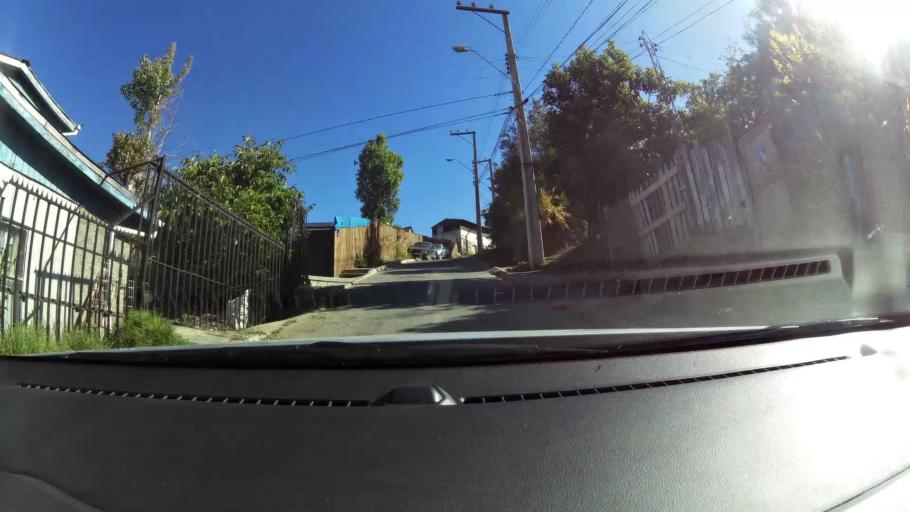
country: CL
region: Valparaiso
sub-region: Provincia de Valparaiso
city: Valparaiso
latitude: -33.0625
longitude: -71.6197
